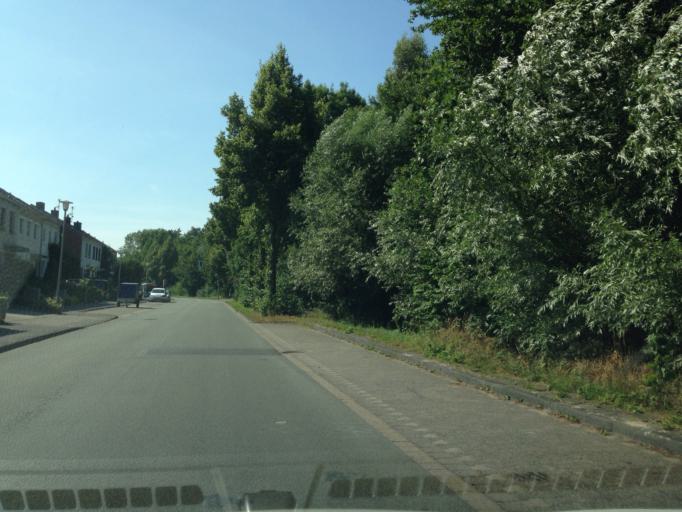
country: DE
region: North Rhine-Westphalia
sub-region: Regierungsbezirk Munster
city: Muenster
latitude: 51.9708
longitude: 7.5711
